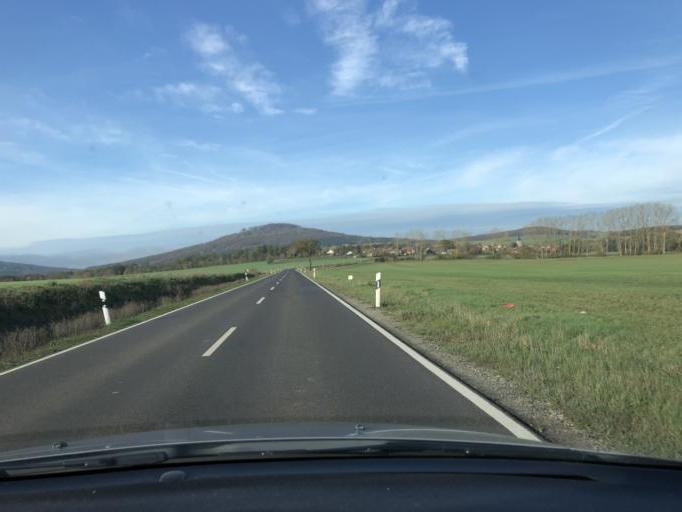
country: DE
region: Thuringia
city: Reurieth
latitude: 50.4102
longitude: 10.6456
